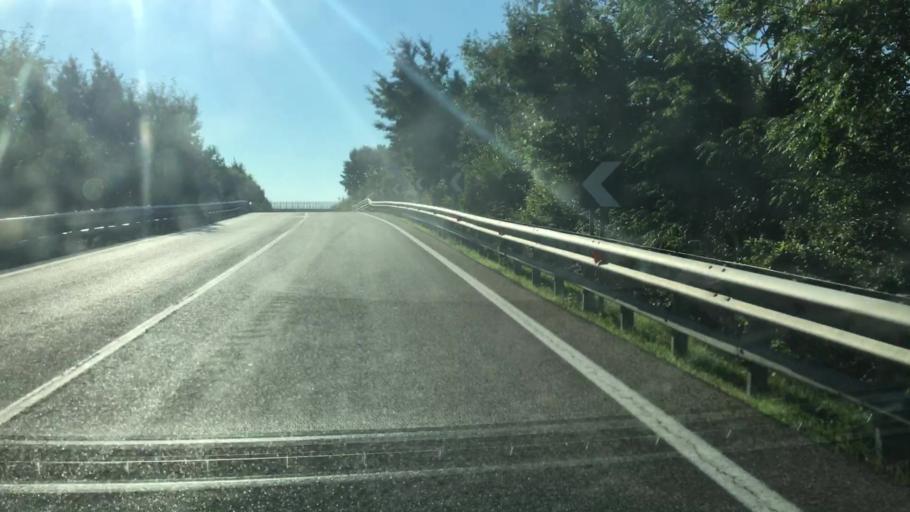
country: IT
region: Molise
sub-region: Provincia di Campobasso
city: Vinchiaturo
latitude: 41.4535
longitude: 14.5841
